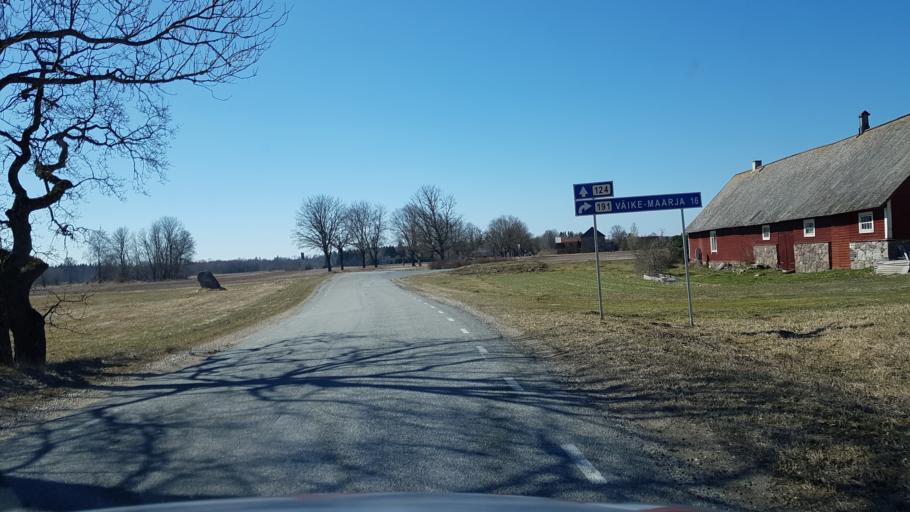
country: EE
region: Laeaene-Virumaa
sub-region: Rakke vald
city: Rakke
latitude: 59.0500
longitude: 26.4180
